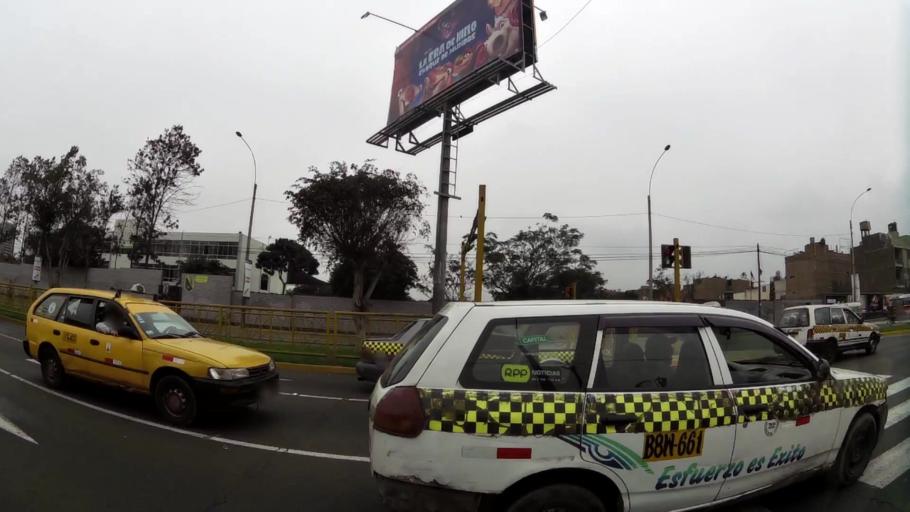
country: PE
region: Lima
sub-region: Lima
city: San Luis
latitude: -12.0816
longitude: -77.0218
